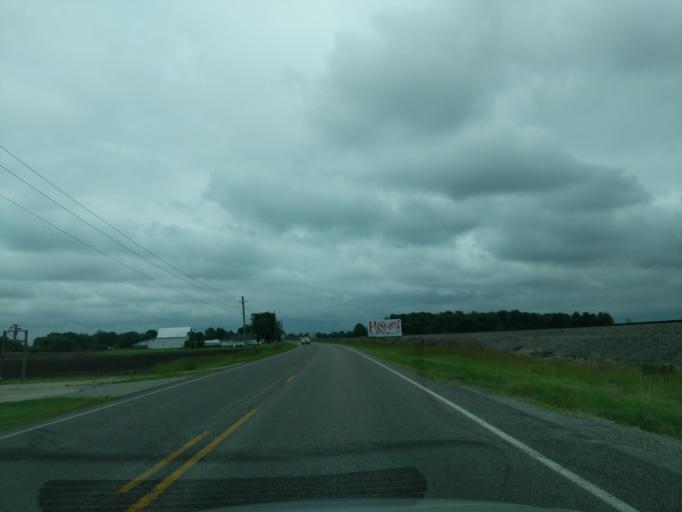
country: US
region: Indiana
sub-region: Madison County
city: Elwood
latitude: 40.2769
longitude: -85.8778
